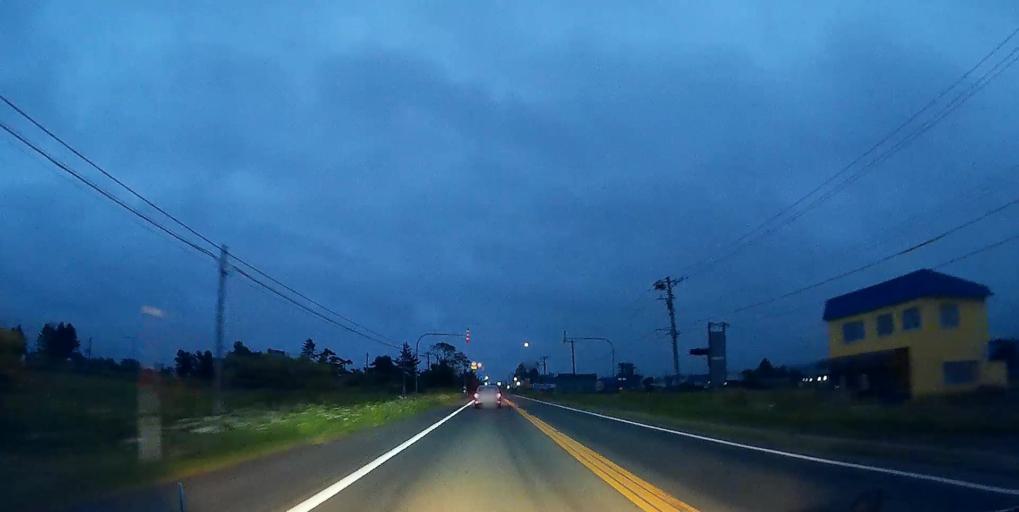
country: JP
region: Hokkaido
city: Nanae
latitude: 42.2202
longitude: 140.3755
